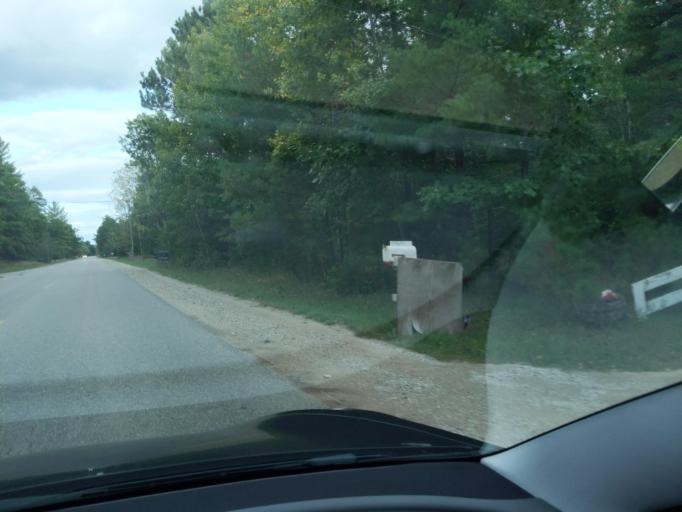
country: US
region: Michigan
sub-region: Kalkaska County
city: Rapid City
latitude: 44.8413
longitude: -85.3008
